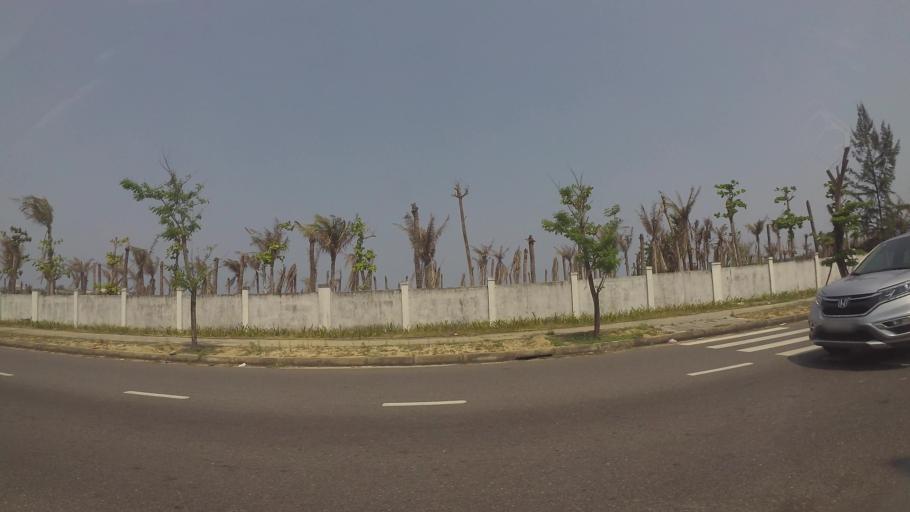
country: VN
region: Da Nang
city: Ngu Hanh Son
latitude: 15.9911
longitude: 108.2702
